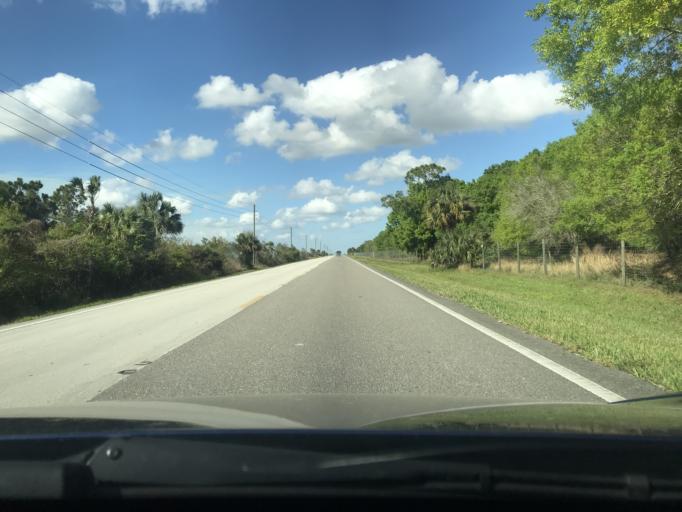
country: US
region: Florida
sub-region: Okeechobee County
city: Taylor Creek
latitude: 27.2321
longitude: -80.6943
